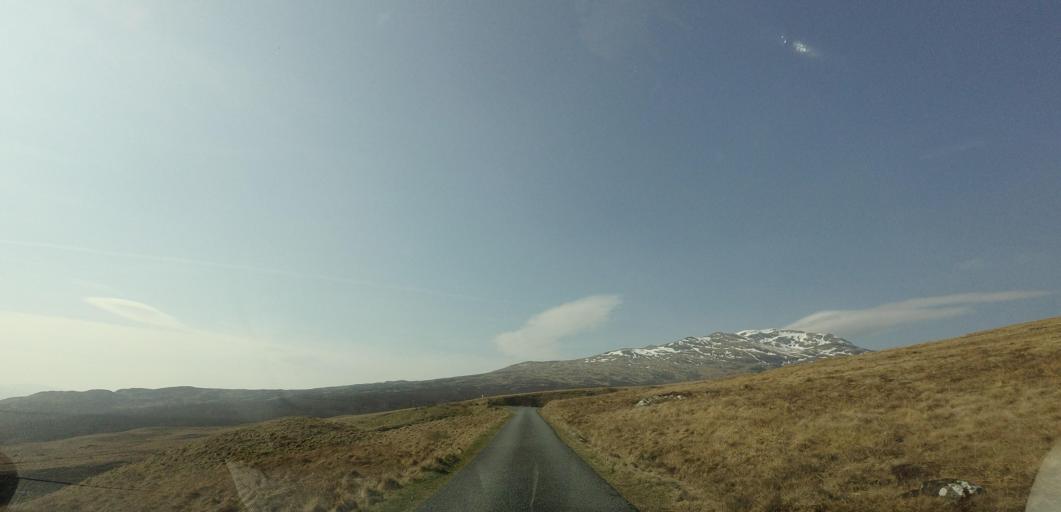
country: GB
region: Scotland
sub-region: Stirling
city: Callander
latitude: 56.5096
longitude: -4.2510
